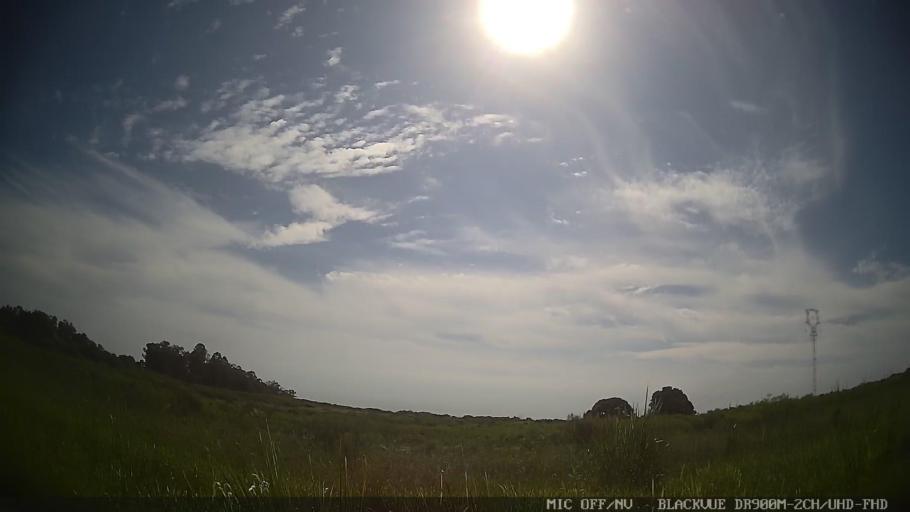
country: BR
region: Sao Paulo
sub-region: Porto Feliz
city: Porto Feliz
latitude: -23.3145
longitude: -47.5323
